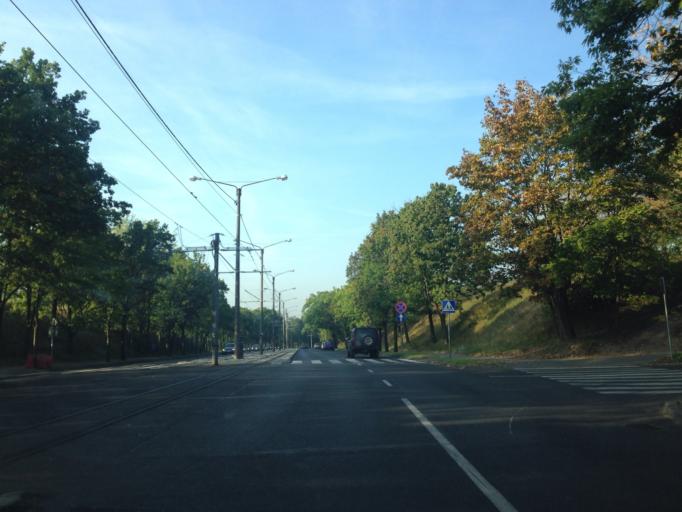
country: PL
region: Kujawsko-Pomorskie
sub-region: Torun
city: Torun
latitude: 53.0138
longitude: 18.6277
